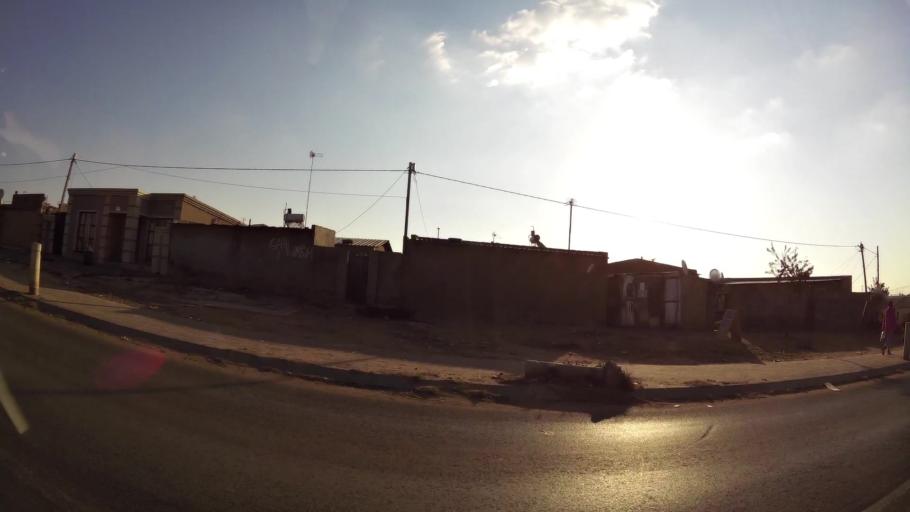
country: ZA
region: Gauteng
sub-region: Ekurhuleni Metropolitan Municipality
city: Tembisa
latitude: -26.0037
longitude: 28.1904
